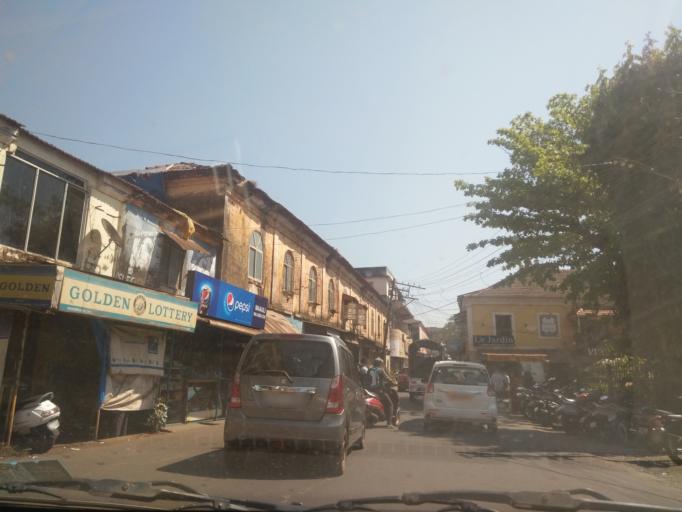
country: IN
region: Goa
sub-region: North Goa
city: Mapuca
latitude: 15.5909
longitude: 73.8105
